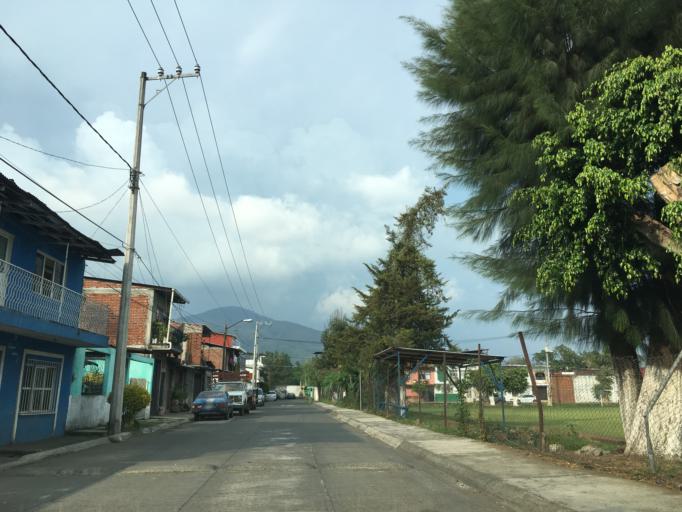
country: MX
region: Michoacan
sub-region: Uruapan
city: Uruapan
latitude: 19.4108
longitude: -102.0497
